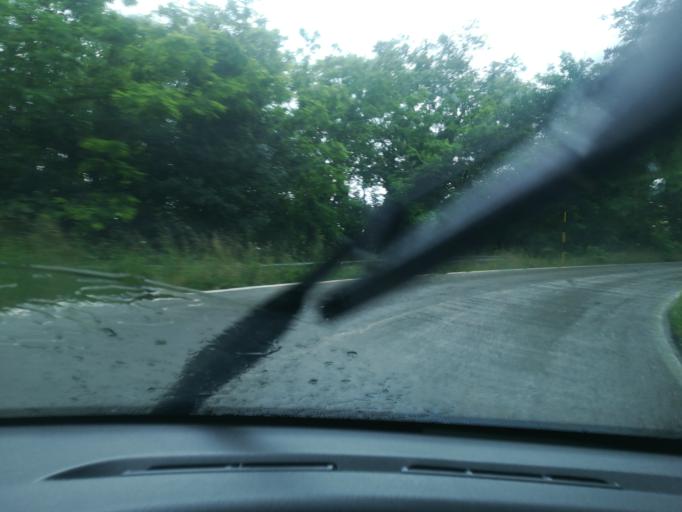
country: IT
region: The Marches
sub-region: Province of Fermo
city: Amandola
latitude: 42.9999
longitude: 13.3388
